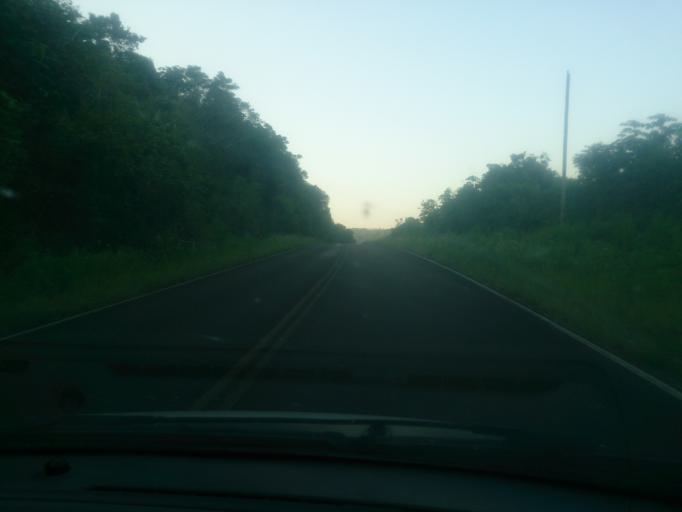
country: AR
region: Misiones
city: Panambi
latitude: -27.6496
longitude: -54.9087
